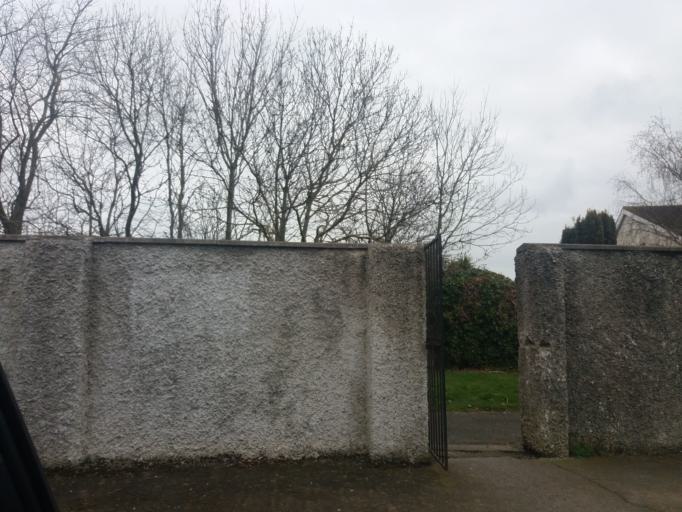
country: IE
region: Leinster
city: Portmarnock
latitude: 53.4216
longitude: -6.1340
